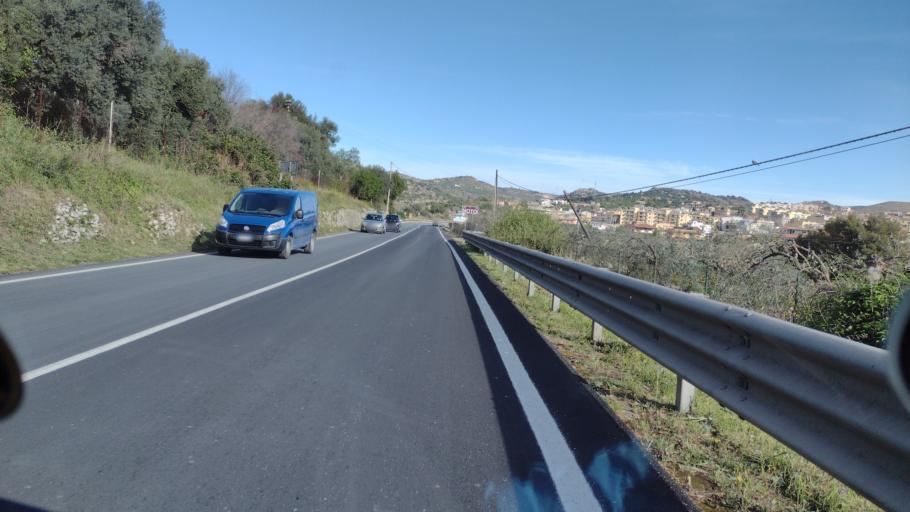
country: IT
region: Sicily
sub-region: Provincia di Siracusa
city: Noto
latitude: 36.8855
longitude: 15.0624
